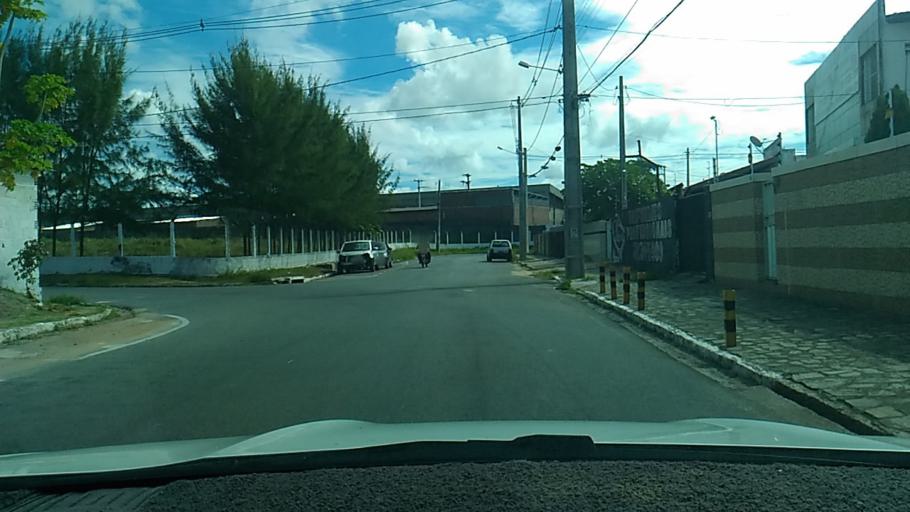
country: BR
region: Paraiba
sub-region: Joao Pessoa
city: Joao Pessoa
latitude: -7.1638
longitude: -34.8638
